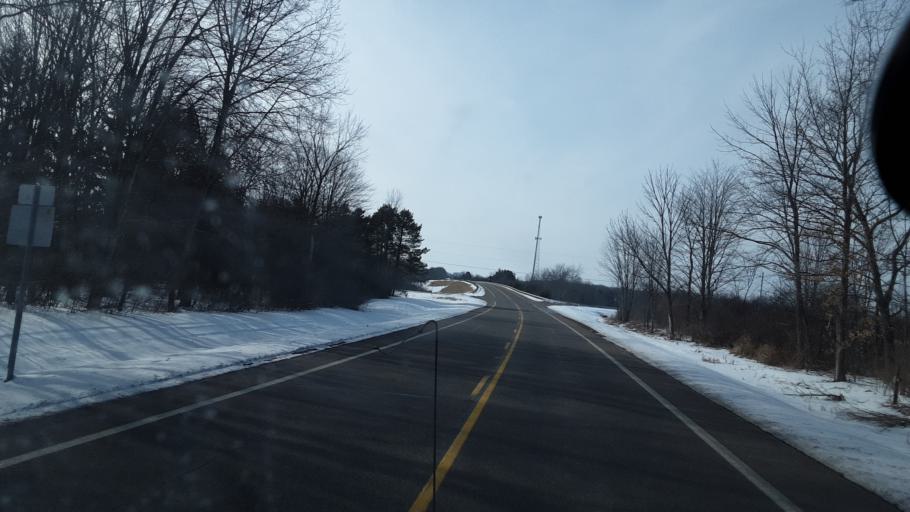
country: US
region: Ohio
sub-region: Stark County
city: Alliance
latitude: 41.0326
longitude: -81.1622
